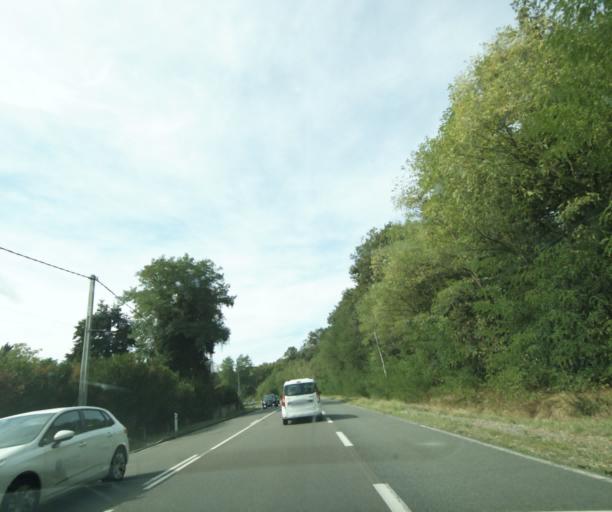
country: FR
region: Auvergne
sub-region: Departement de l'Allier
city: Bellerive-sur-Allier
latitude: 46.1287
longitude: 3.3761
